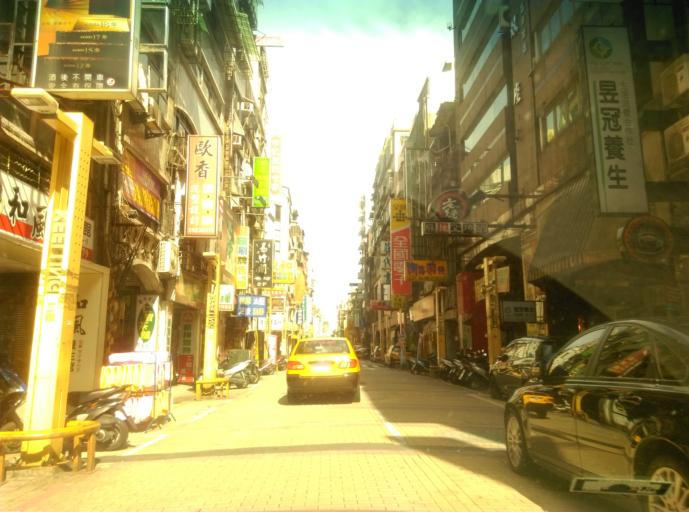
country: TW
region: Taiwan
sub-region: Keelung
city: Keelung
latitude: 25.1317
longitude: 121.7460
